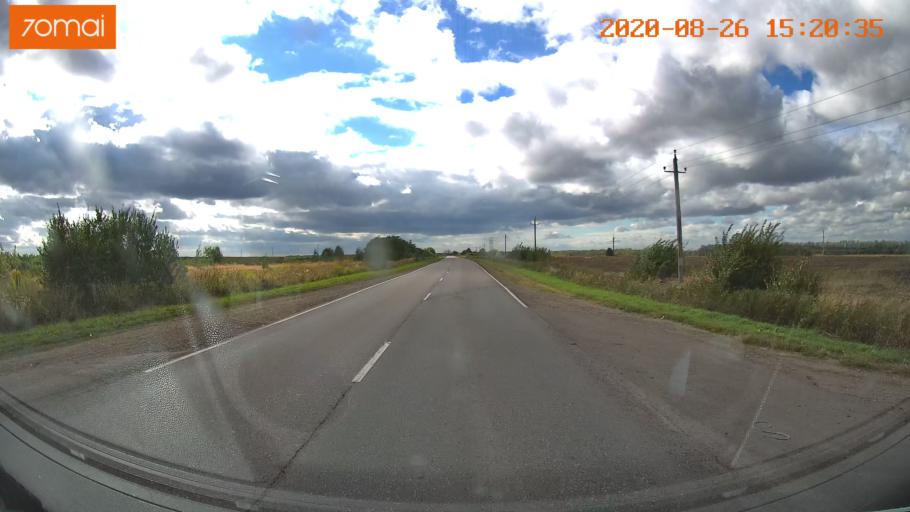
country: RU
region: Tula
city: Severo-Zadonsk
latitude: 54.1432
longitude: 38.4925
